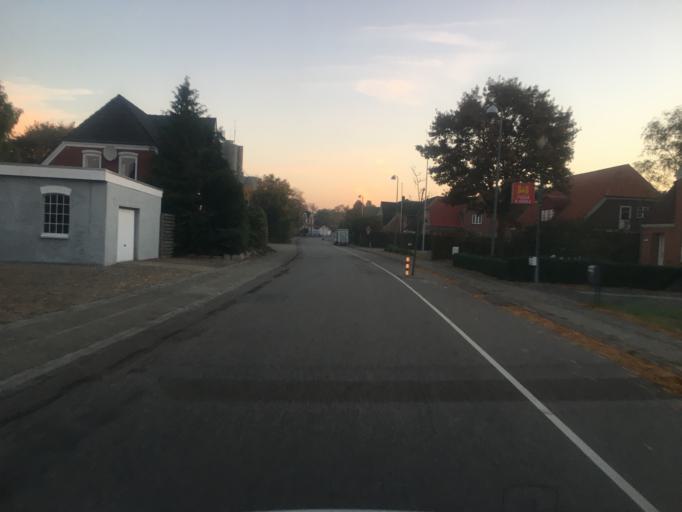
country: DE
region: Schleswig-Holstein
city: Bramstedtlund
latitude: 54.9402
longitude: 9.0846
